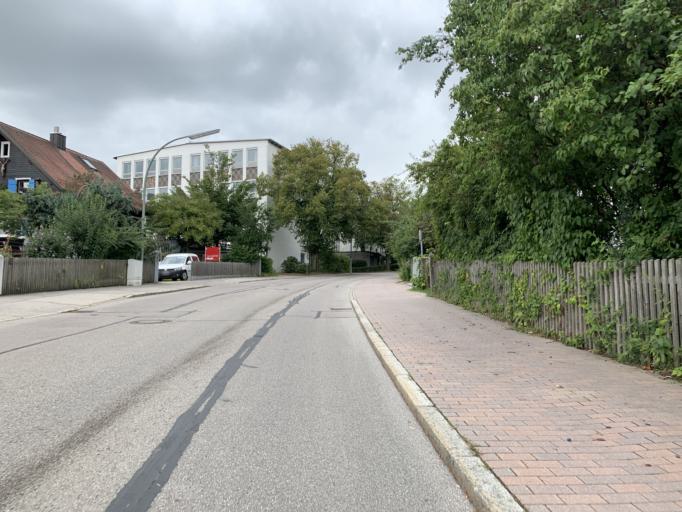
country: DE
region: Bavaria
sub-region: Upper Bavaria
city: Freising
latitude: 48.4062
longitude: 11.7444
